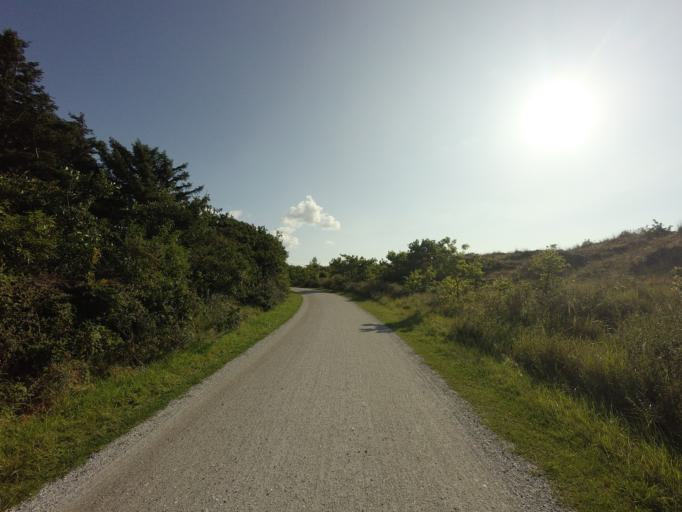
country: NL
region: Friesland
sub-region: Gemeente Terschelling
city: West-Terschelling
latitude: 53.3874
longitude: 5.2283
